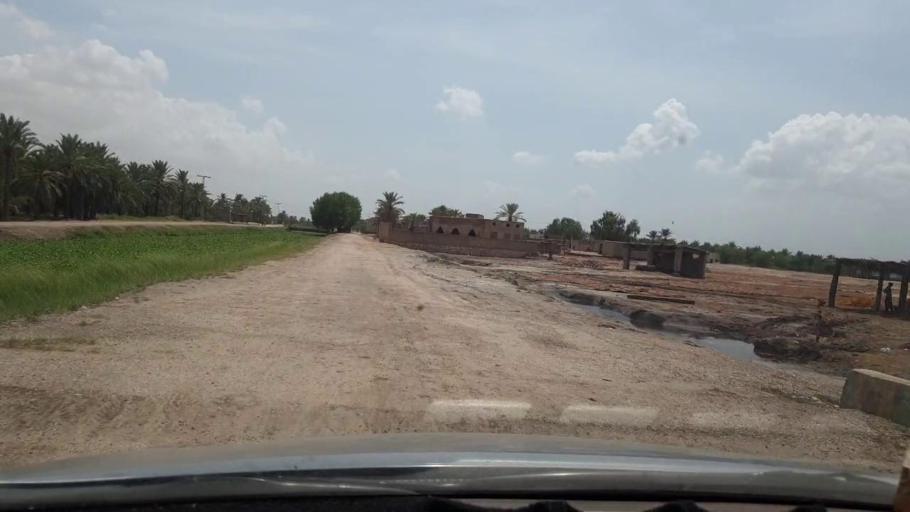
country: PK
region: Sindh
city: Khairpur
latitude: 27.4526
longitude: 68.7879
